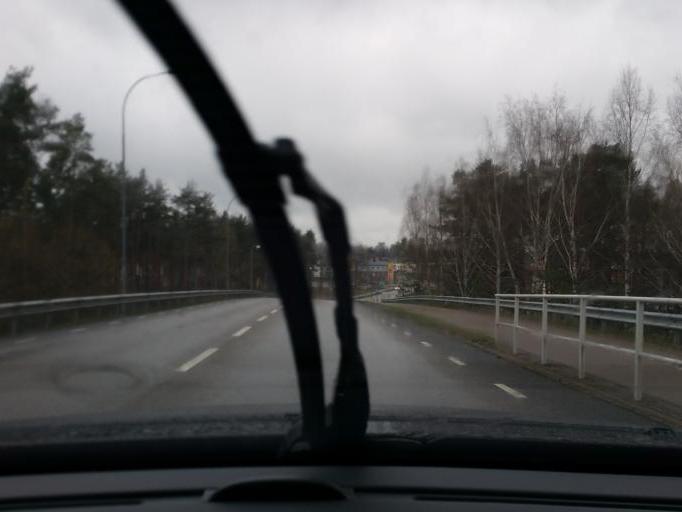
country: SE
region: Kronoberg
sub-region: Vaxjo Kommun
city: Lammhult
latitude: 57.1677
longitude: 14.5851
